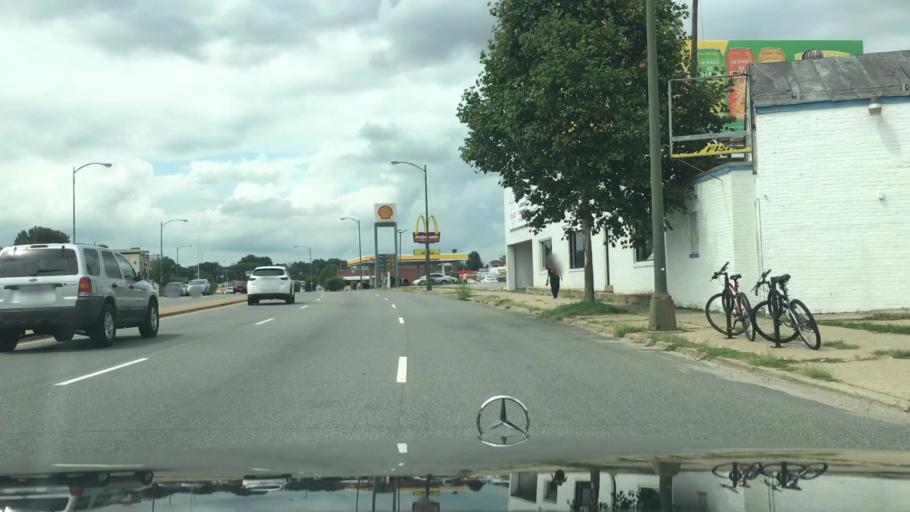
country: US
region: Virginia
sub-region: City of Richmond
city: Richmond
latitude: 37.5614
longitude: -77.4426
